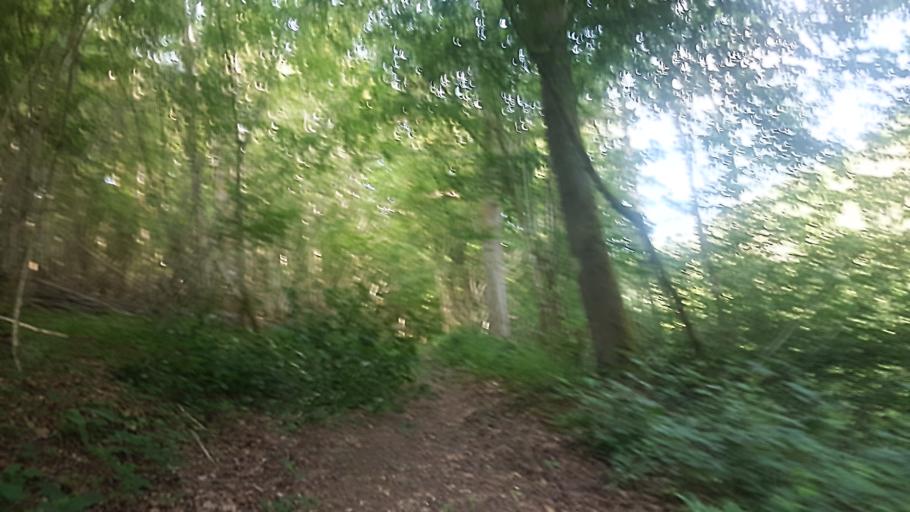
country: BE
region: Wallonia
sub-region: Province de Namur
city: Couvin
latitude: 50.0463
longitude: 4.5859
